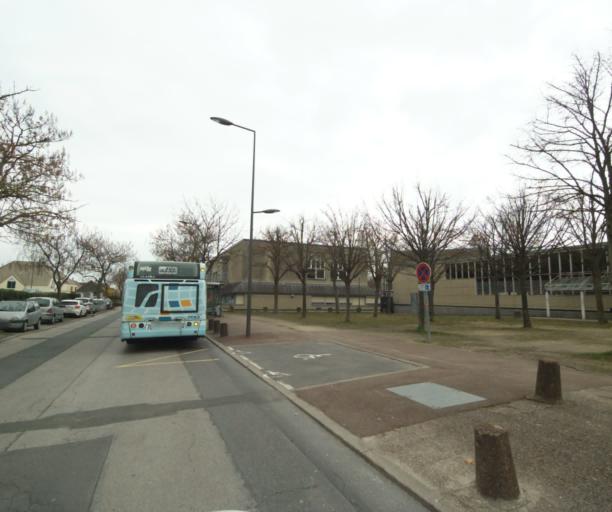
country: FR
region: Ile-de-France
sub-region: Departement du Val-d'Oise
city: Vaureal
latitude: 49.0448
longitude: 2.0312
